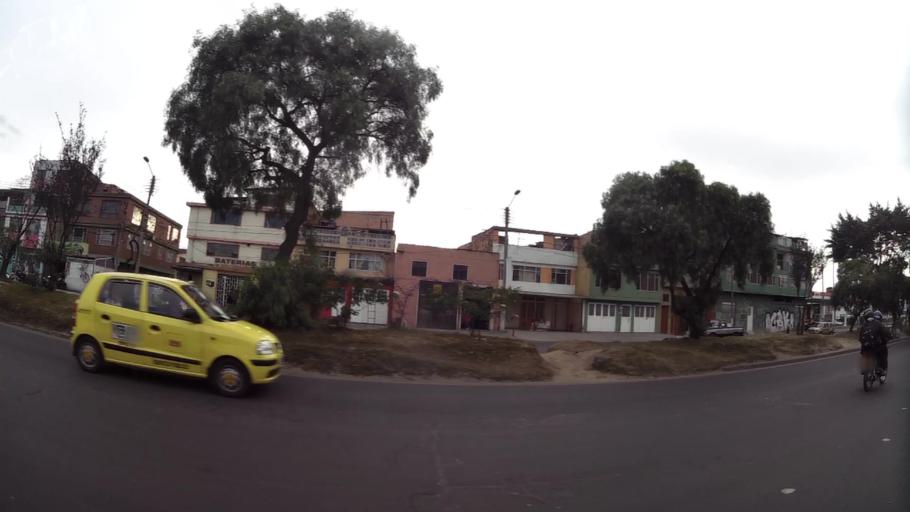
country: CO
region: Cundinamarca
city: Soacha
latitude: 4.6170
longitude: -74.1635
